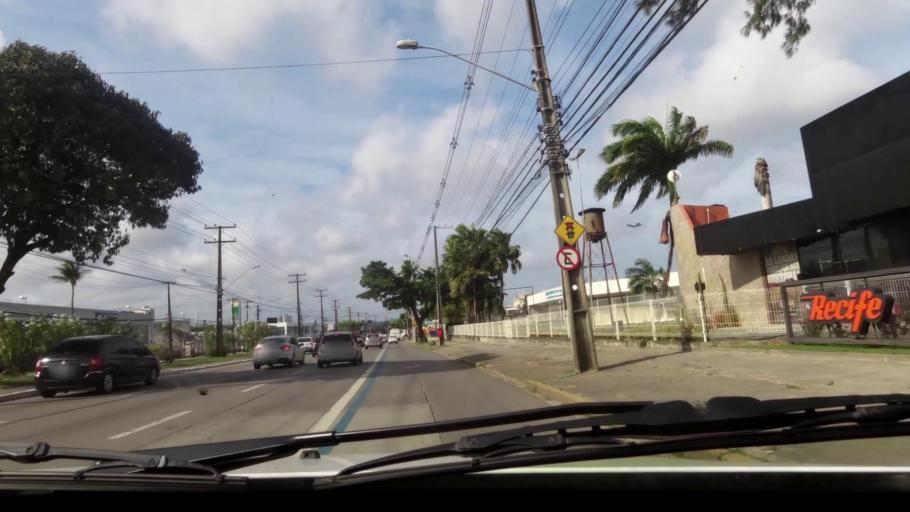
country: BR
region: Pernambuco
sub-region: Recife
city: Recife
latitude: -8.0988
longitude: -34.9100
